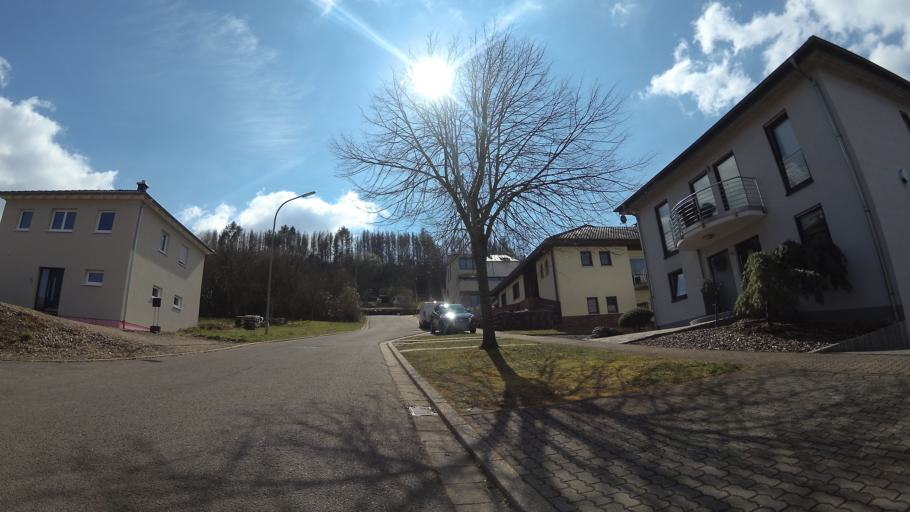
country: DE
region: Saarland
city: Rehlingen-Siersburg
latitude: 49.3509
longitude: 6.6177
